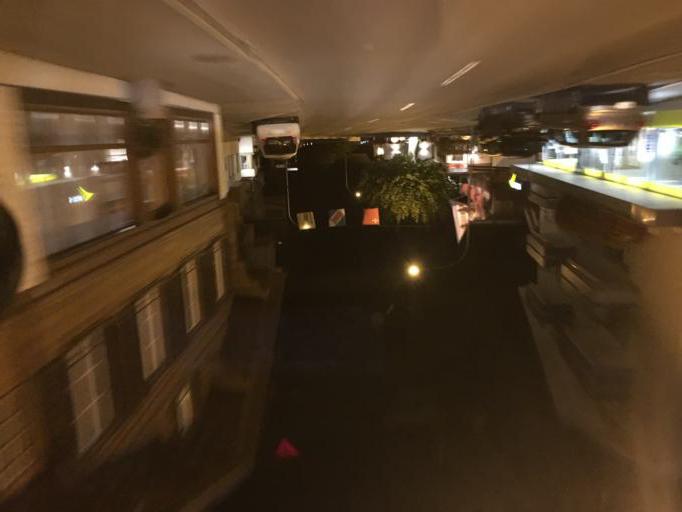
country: CH
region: Bern
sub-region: Interlaken-Oberhasli District
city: Brienz
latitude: 46.7542
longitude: 8.0341
